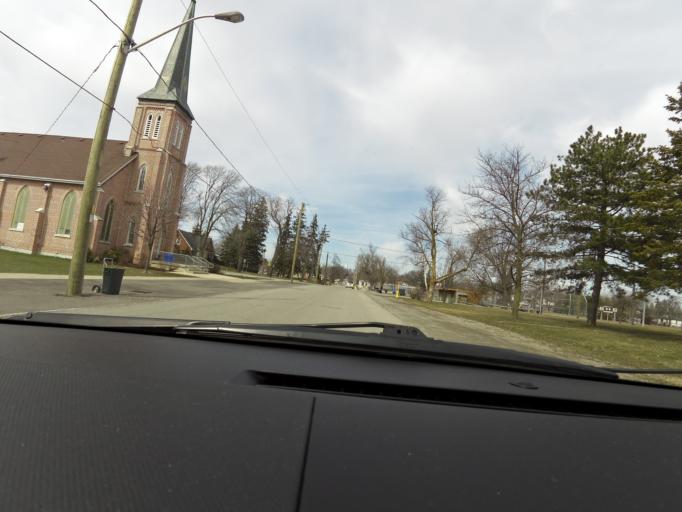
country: CA
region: Ontario
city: Ancaster
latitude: 42.9477
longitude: -79.8561
